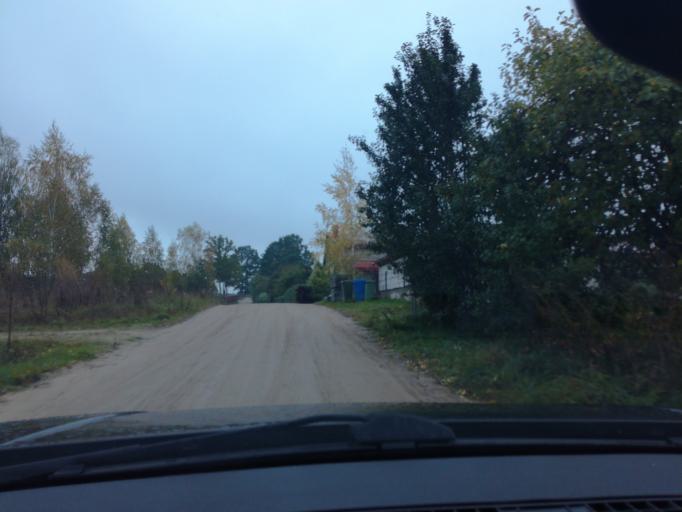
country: LT
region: Alytaus apskritis
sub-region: Alytus
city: Alytus
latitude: 54.3940
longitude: 24.0991
